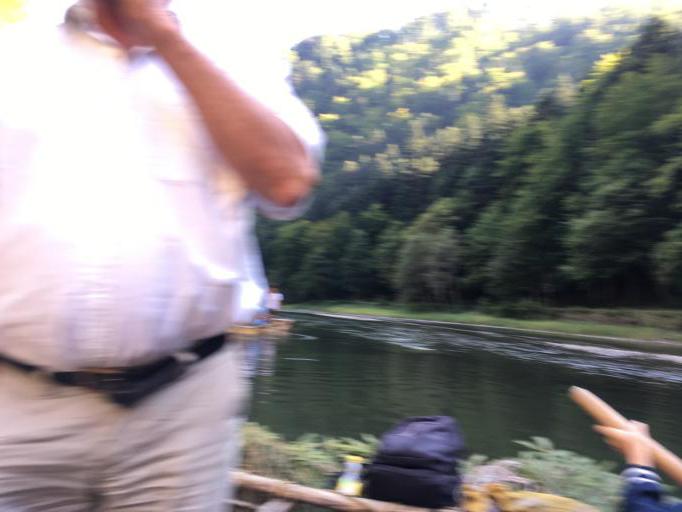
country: PL
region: Lesser Poland Voivodeship
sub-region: Powiat nowotarski
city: Kroscienko nad Dunajcem
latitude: 49.4167
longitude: 20.4373
